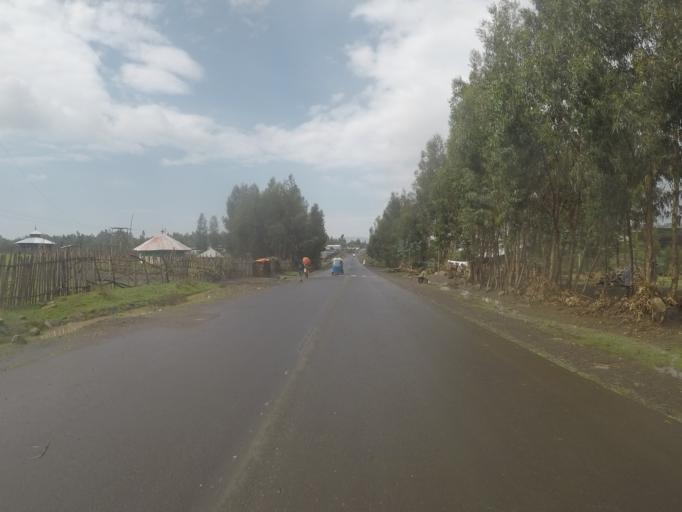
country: ET
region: Amhara
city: Debark'
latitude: 13.1221
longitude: 37.8832
